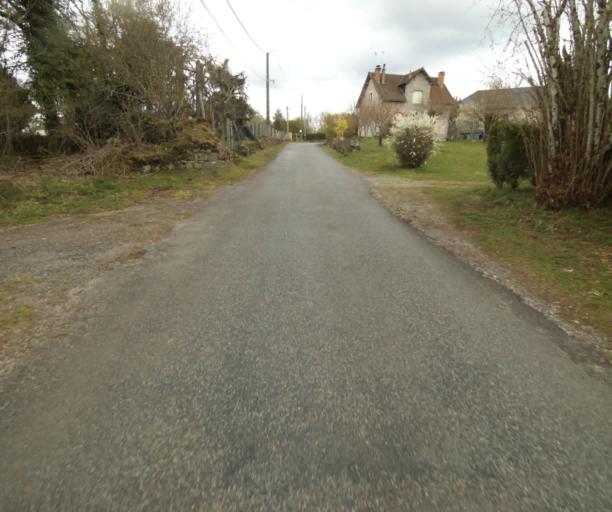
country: FR
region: Limousin
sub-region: Departement de la Correze
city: Correze
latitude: 45.3267
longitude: 1.9370
